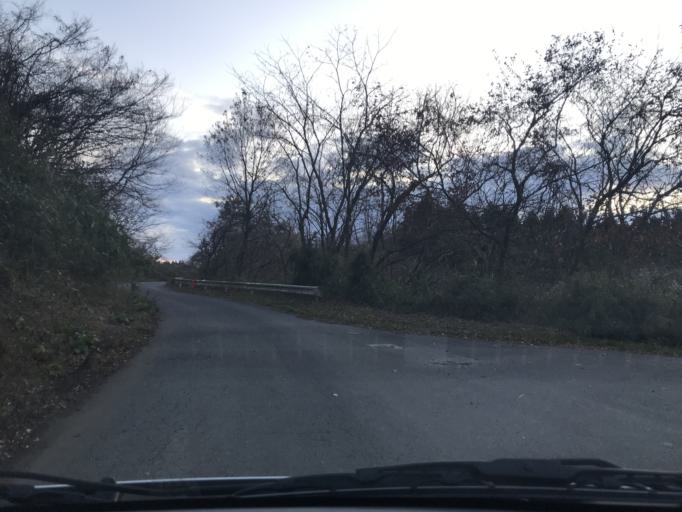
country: JP
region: Iwate
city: Ichinoseki
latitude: 38.8295
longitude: 141.0920
